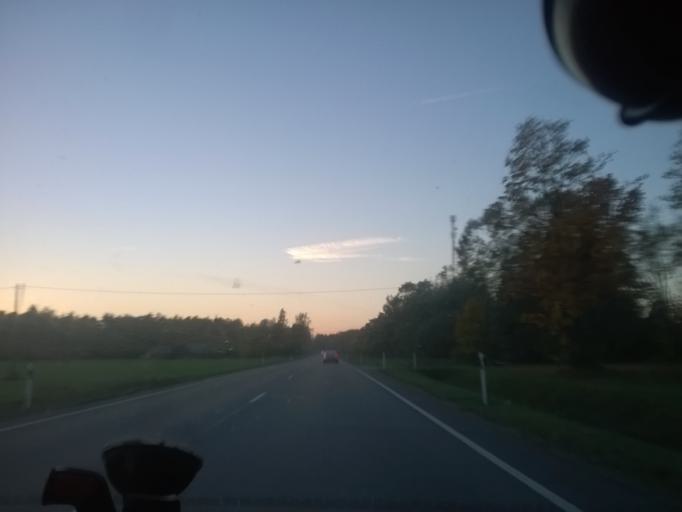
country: EE
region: Laeaene
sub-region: Ridala Parish
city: Uuemoisa
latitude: 58.9601
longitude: 23.7071
